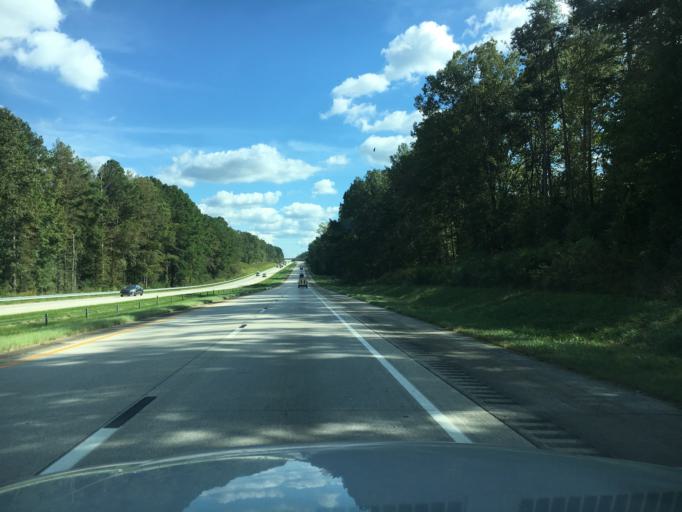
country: US
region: South Carolina
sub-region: Laurens County
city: Laurens
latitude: 34.5932
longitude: -82.0538
